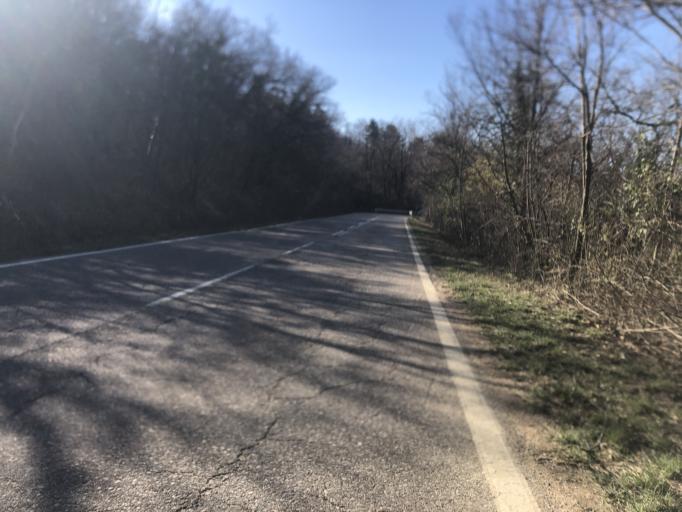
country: IT
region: Veneto
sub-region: Provincia di Verona
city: Volargne
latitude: 45.5541
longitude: 10.8443
